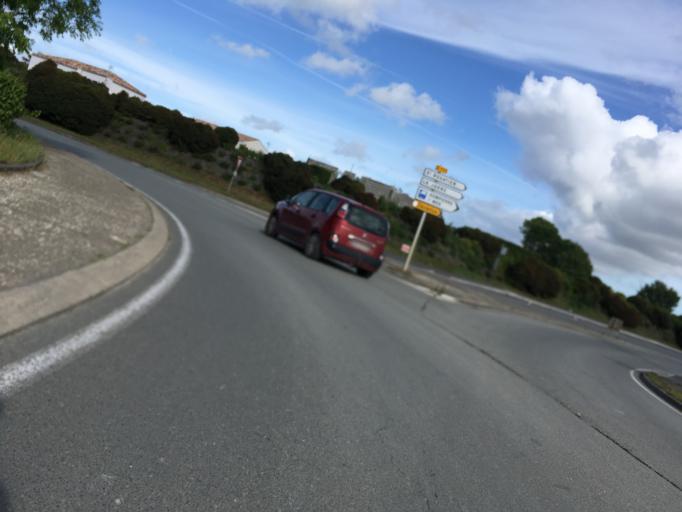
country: FR
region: Poitou-Charentes
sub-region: Departement de la Charente-Maritime
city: Dompierre-sur-Mer
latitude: 46.1745
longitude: -1.0653
